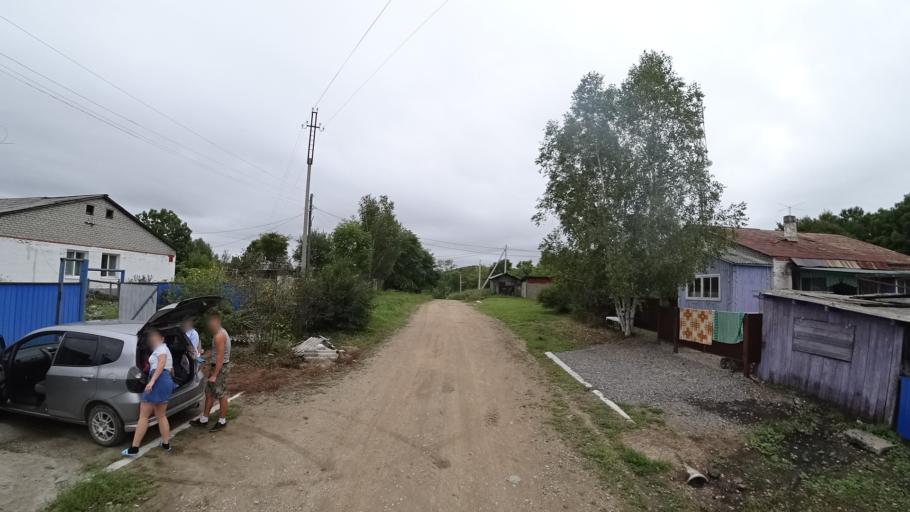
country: RU
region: Primorskiy
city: Rettikhovka
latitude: 44.1632
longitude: 132.7491
